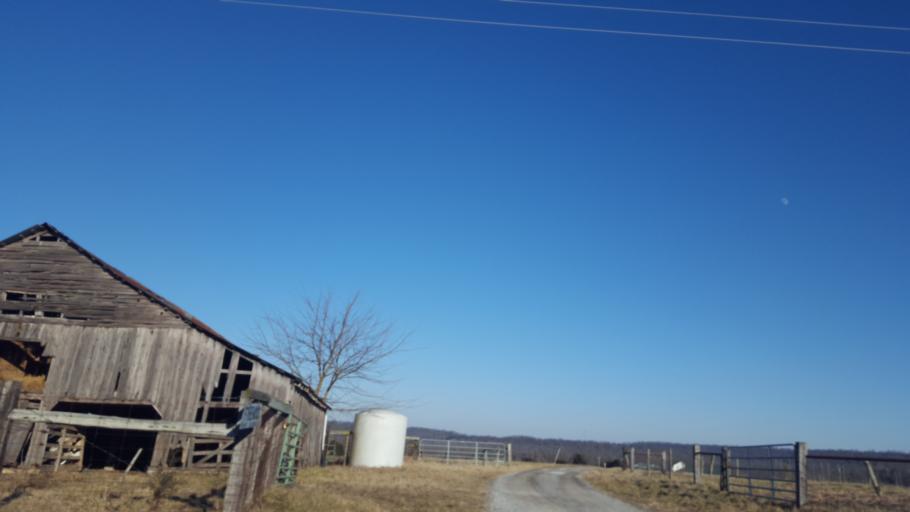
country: US
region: Kentucky
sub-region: Crittenden County
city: Marion
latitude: 37.4387
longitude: -88.0526
